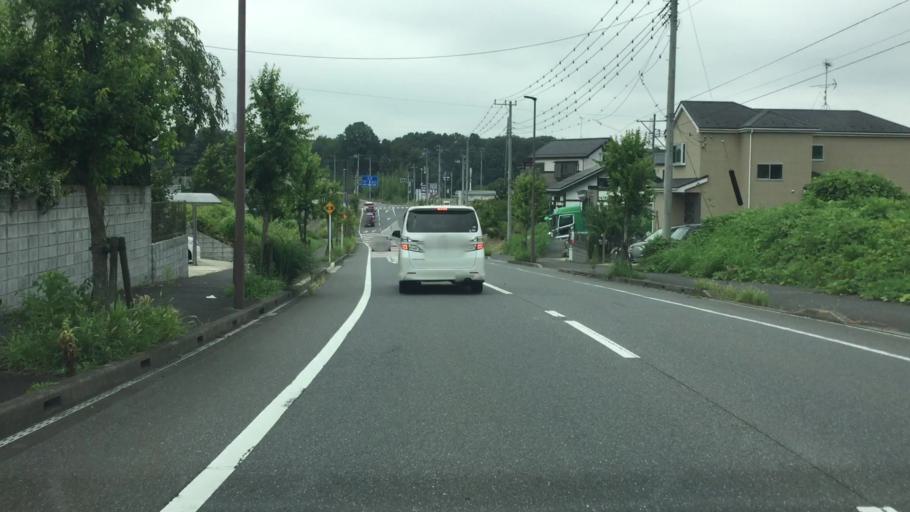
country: JP
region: Chiba
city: Abiko
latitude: 35.8432
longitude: 140.0165
